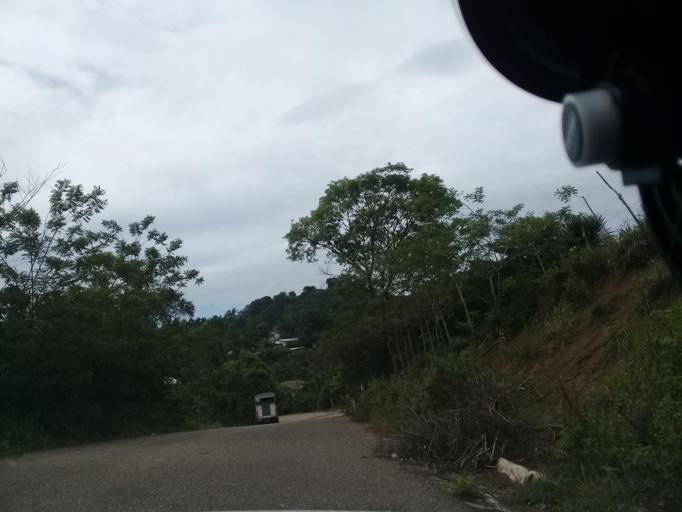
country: MX
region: Veracruz
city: Platon Sanchez
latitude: 21.2148
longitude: -98.3682
